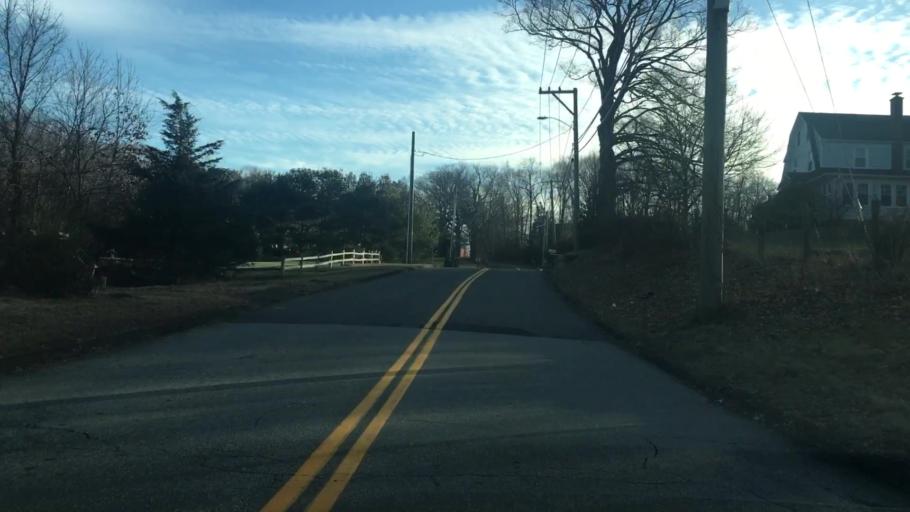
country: US
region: Connecticut
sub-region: Middlesex County
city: Middletown
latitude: 41.5206
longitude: -72.6492
